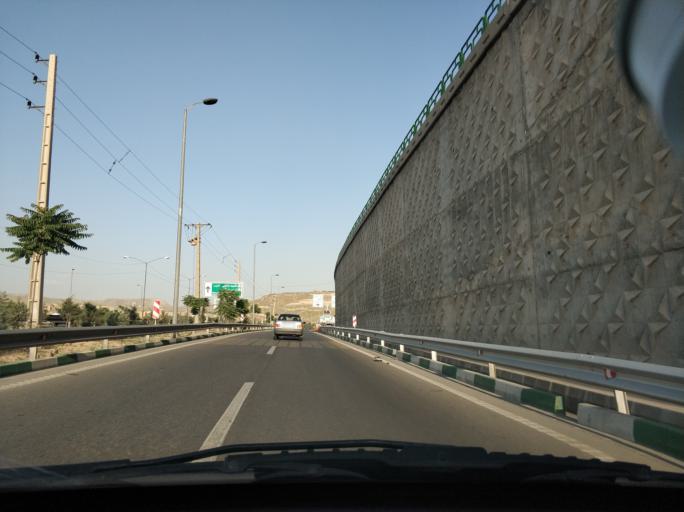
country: IR
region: Tehran
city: Tajrish
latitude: 35.7443
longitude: 51.6042
